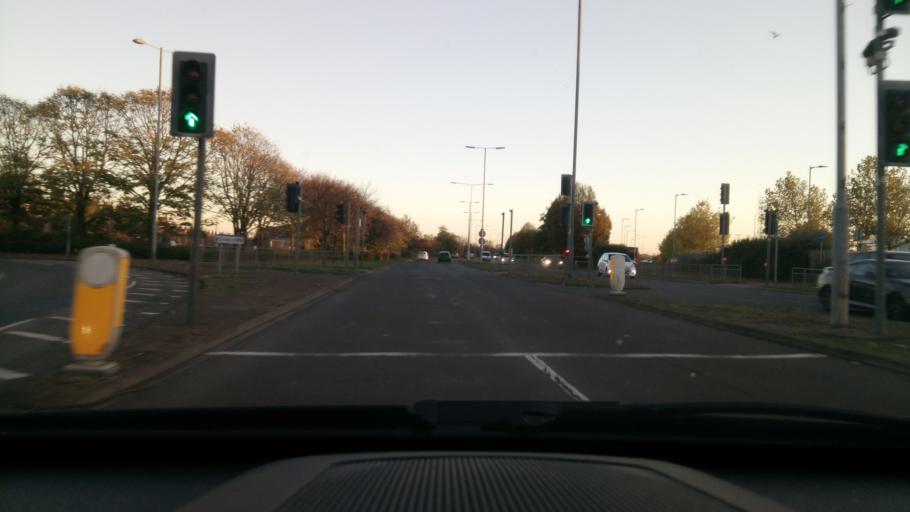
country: GB
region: England
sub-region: Peterborough
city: Peterborough
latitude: 52.5950
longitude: -0.2597
